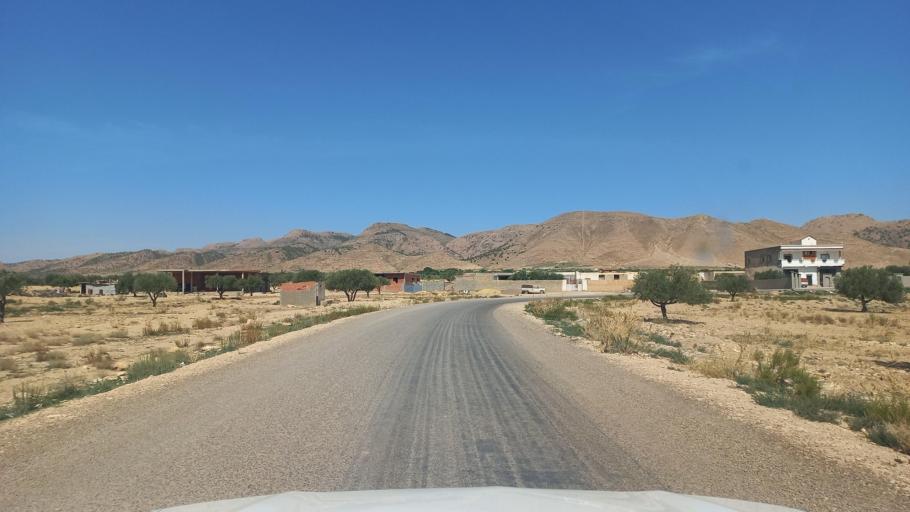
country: TN
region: Al Qasrayn
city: Sbiba
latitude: 35.4413
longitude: 9.0741
